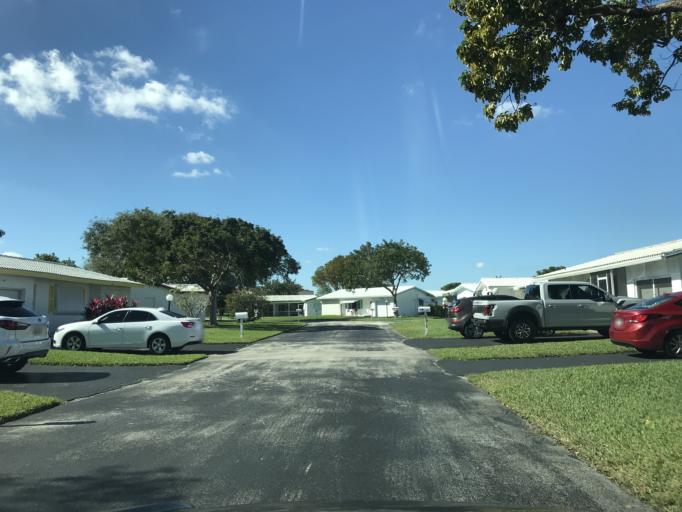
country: US
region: Florida
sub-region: Broward County
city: Plantation
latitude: 26.1400
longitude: -80.2603
